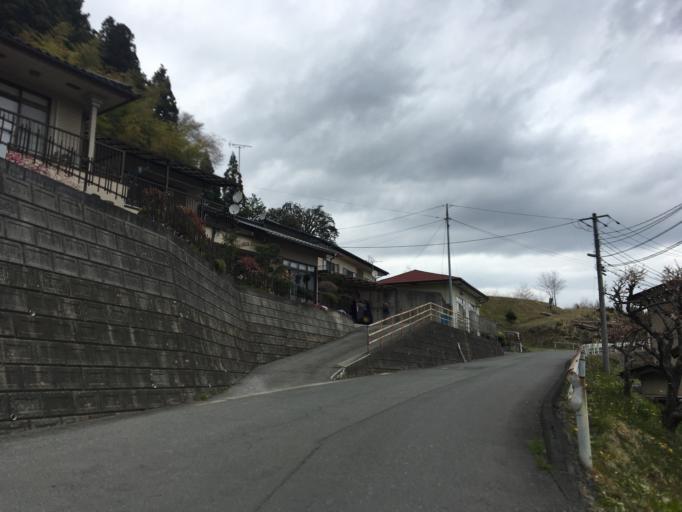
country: JP
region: Iwate
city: Ofunato
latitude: 38.9141
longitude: 141.5779
